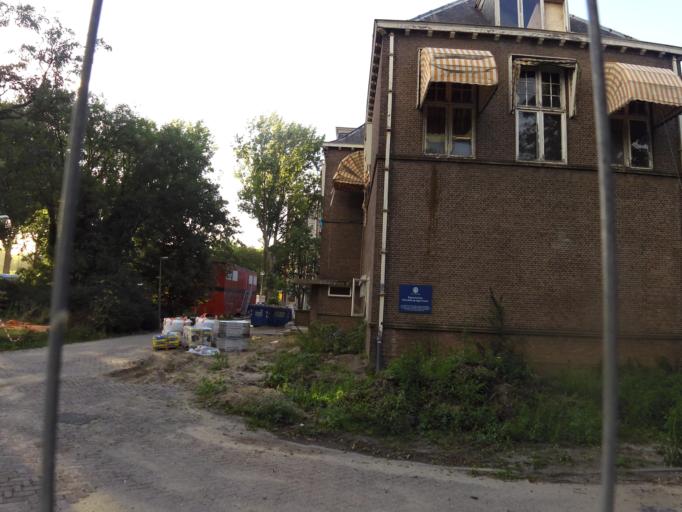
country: NL
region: South Holland
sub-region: Gemeente Oegstgeest
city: Oegstgeest
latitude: 52.1674
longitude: 4.4743
